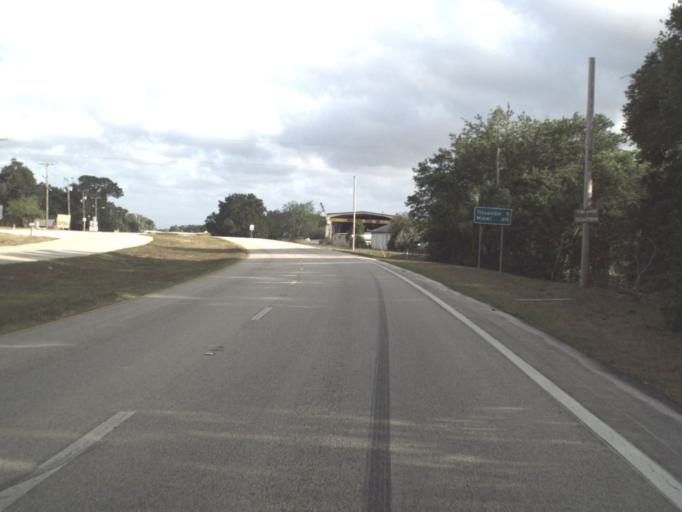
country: US
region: Florida
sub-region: Brevard County
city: Mims
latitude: 28.6590
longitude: -80.8430
